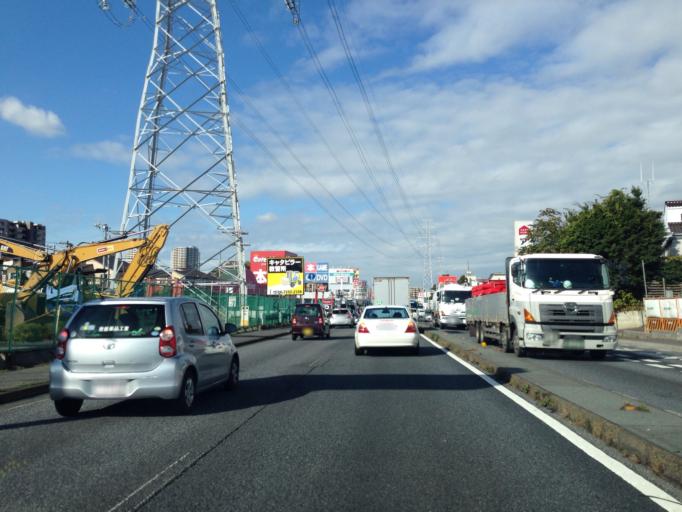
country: JP
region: Chiba
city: Kashiwa
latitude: 35.8843
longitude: 139.9641
